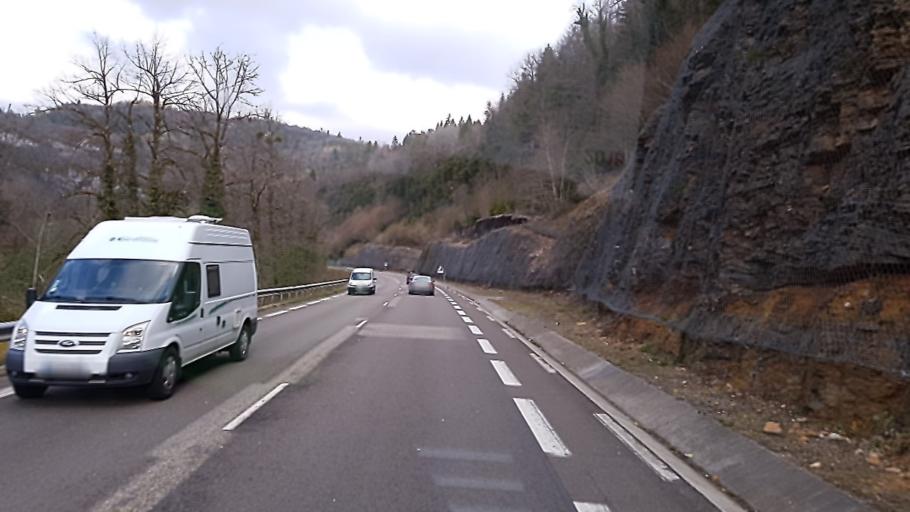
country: FR
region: Franche-Comte
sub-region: Departement du Jura
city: Lavans-les-Saint-Claude
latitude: 46.3620
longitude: 5.7976
